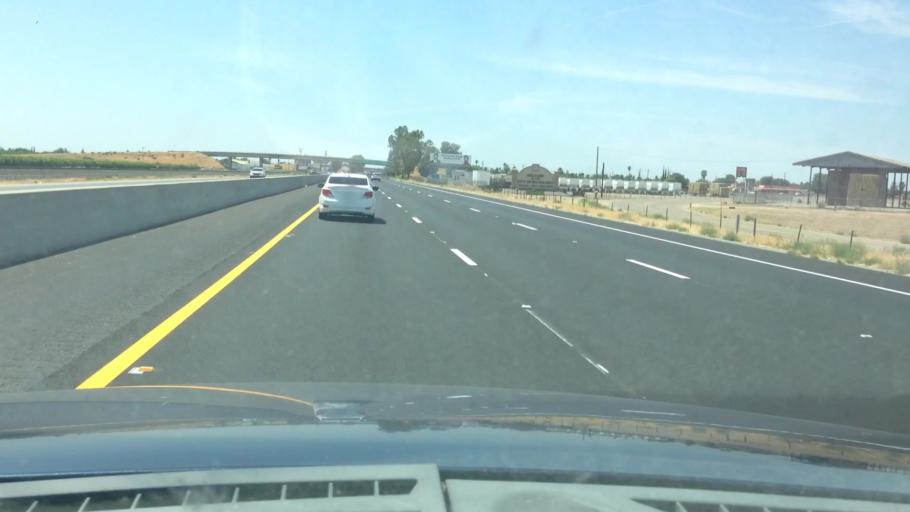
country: US
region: California
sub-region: Kern County
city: McFarland
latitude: 35.6940
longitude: -119.2309
